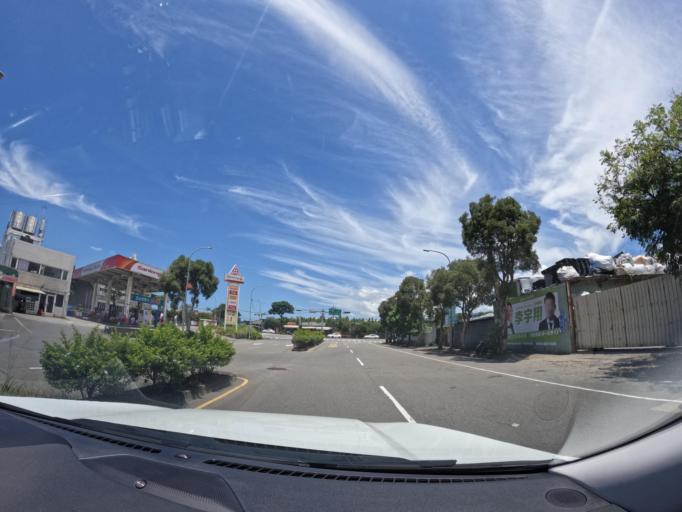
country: TW
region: Taipei
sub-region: Taipei
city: Banqiao
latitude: 25.0900
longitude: 121.3837
